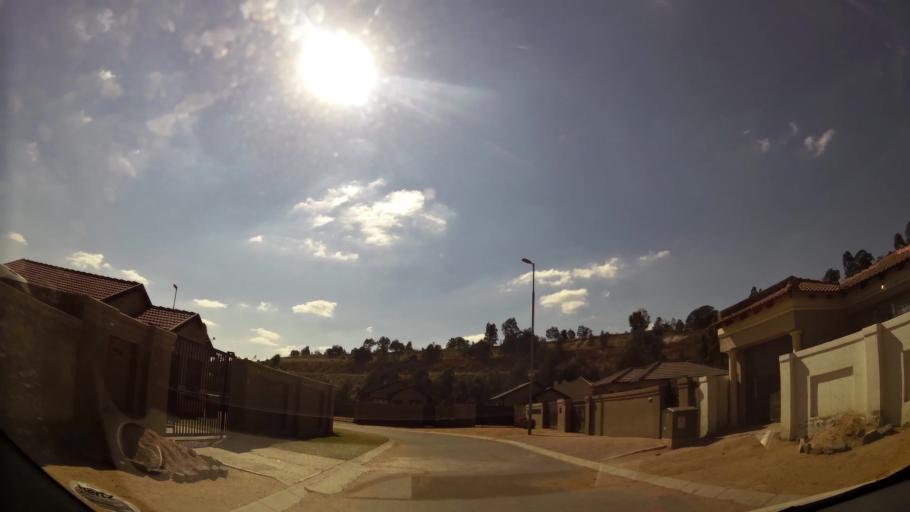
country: ZA
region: Gauteng
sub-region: West Rand District Municipality
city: Krugersdorp
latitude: -26.1461
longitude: 27.7743
